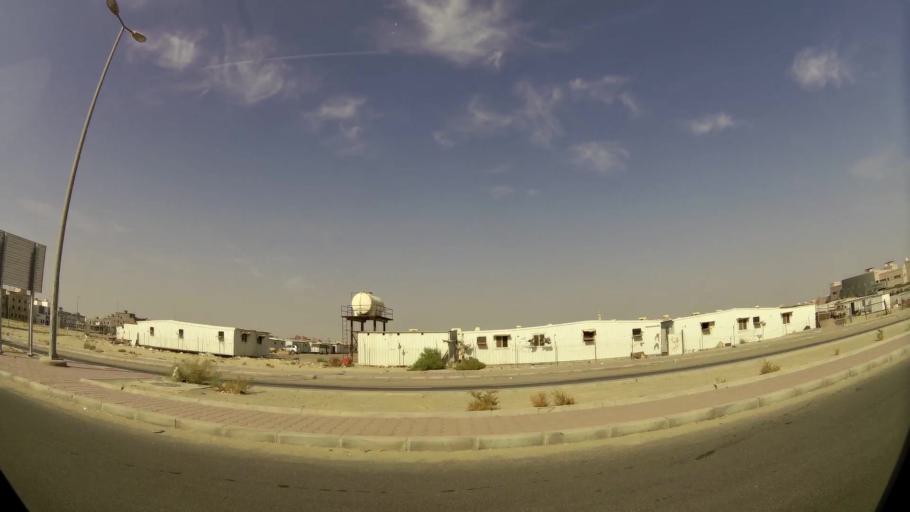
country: KW
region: Al Ahmadi
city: Al Wafrah
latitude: 28.7986
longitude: 48.0606
